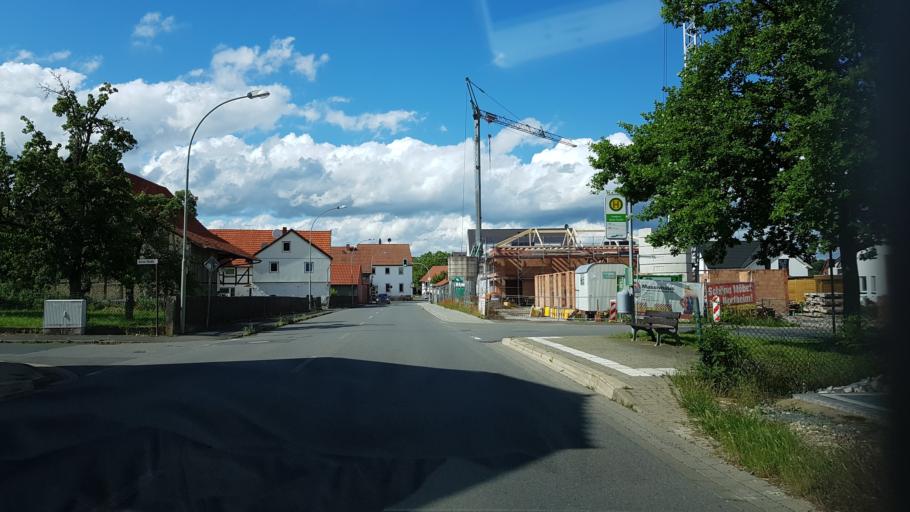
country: DE
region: Lower Saxony
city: Bovenden
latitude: 51.5817
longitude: 9.8746
